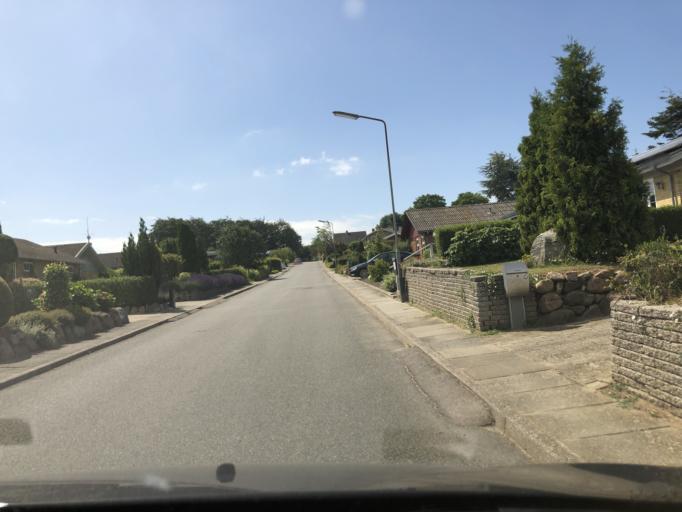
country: DK
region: South Denmark
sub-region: Faaborg-Midtfyn Kommune
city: Faaborg
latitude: 54.9397
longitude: 10.2610
